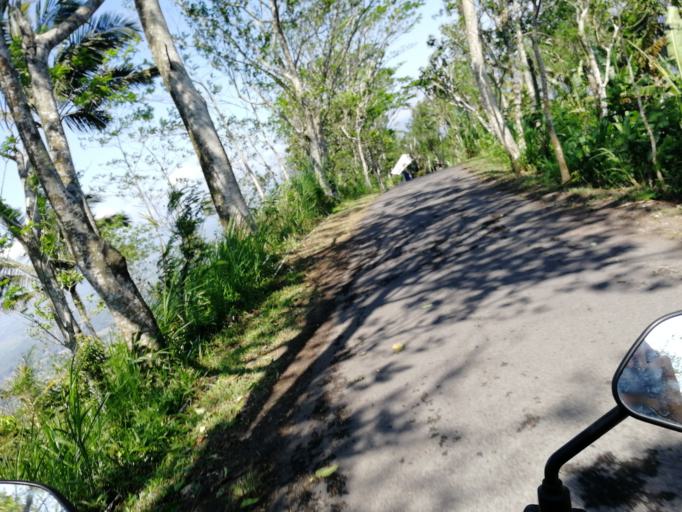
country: ID
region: Bali
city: Tiyingtali Kelod
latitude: -8.3922
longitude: 115.6352
